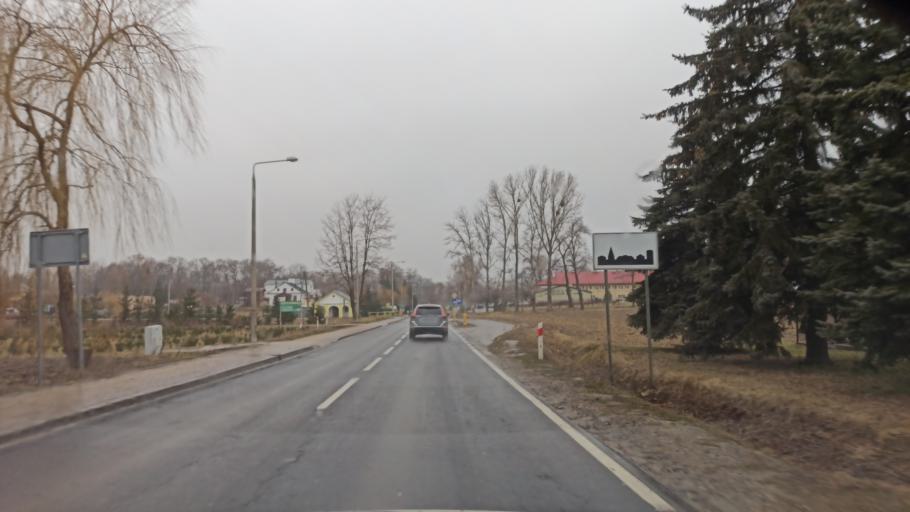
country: PL
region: Lublin Voivodeship
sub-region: Powiat lubelski
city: Strzyzowice
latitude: 51.0488
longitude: 22.4506
